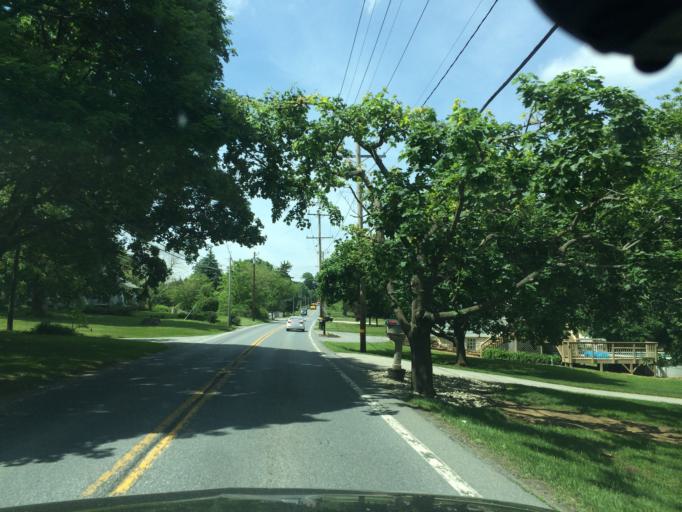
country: US
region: Maryland
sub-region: Carroll County
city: Eldersburg
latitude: 39.4611
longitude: -76.9321
